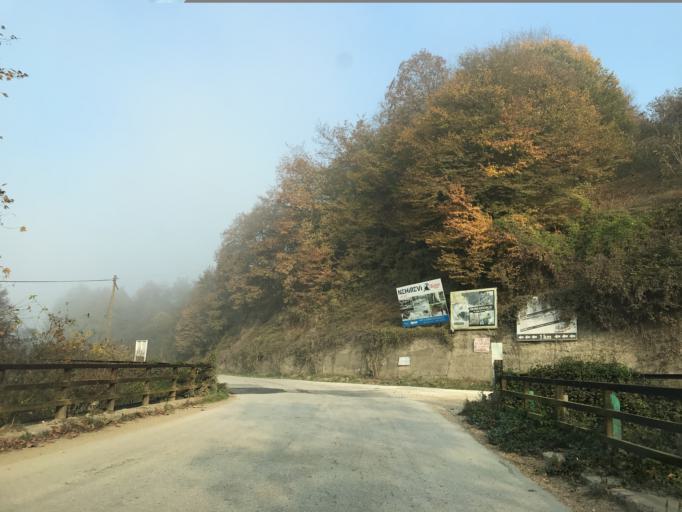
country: TR
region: Duzce
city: Cumayeri
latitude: 40.8949
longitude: 30.9561
